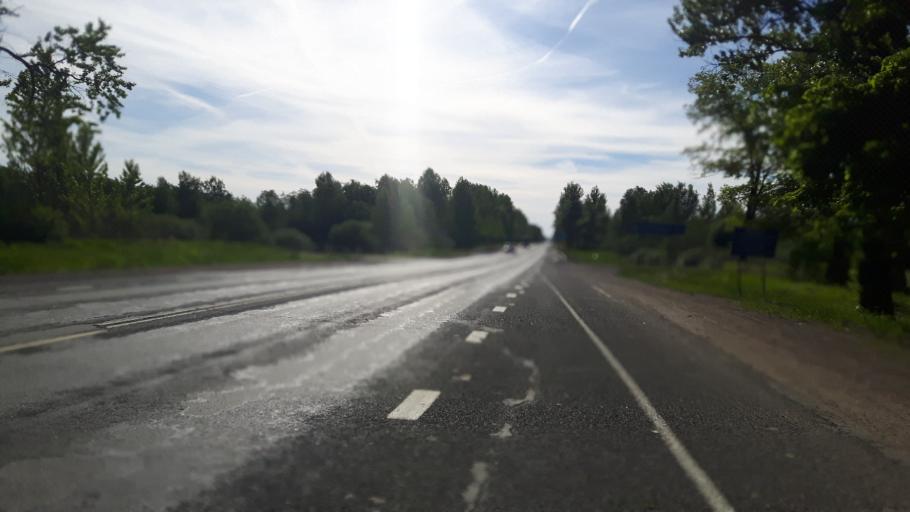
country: RU
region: Leningrad
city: Ivangorod
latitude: 59.3810
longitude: 28.3304
